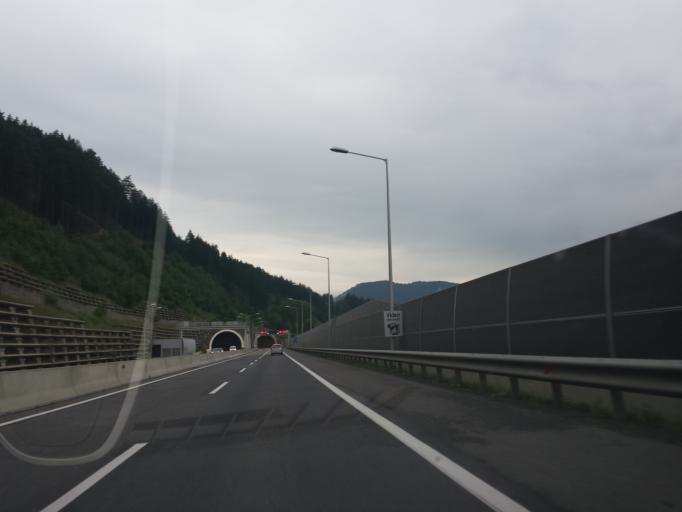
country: AT
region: Styria
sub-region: Politischer Bezirk Bruck-Muerzzuschlag
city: Pernegg an der Mur
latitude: 47.3524
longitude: 15.3422
